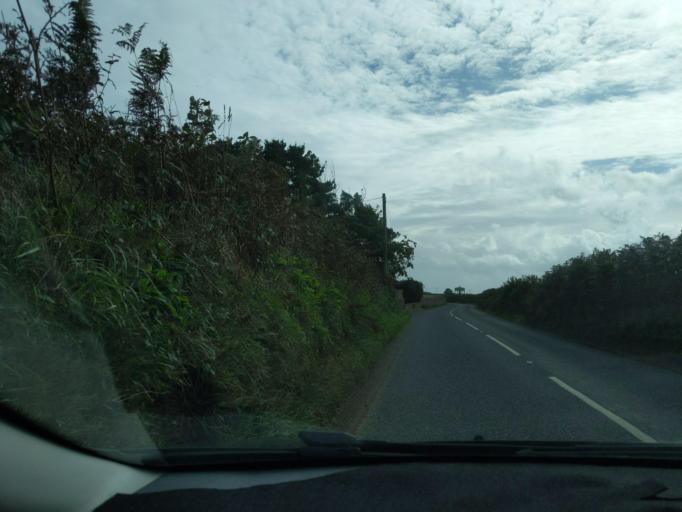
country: GB
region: England
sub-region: Cornwall
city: Mevagissey
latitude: 50.2673
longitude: -4.8300
